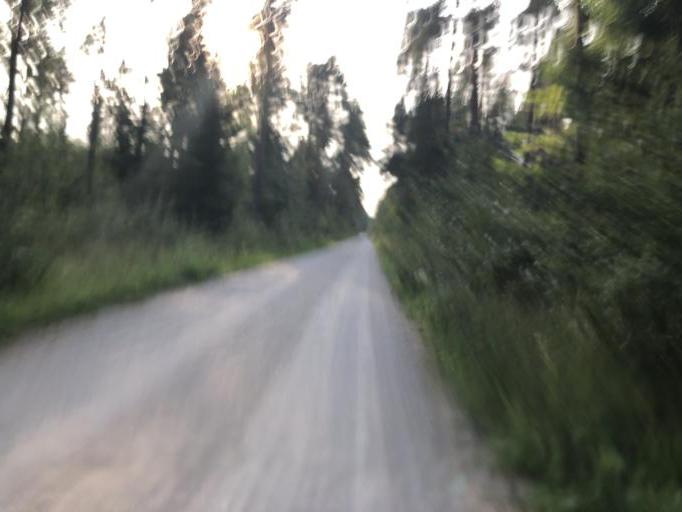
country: DE
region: Bavaria
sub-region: Regierungsbezirk Mittelfranken
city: Buckenhof
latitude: 49.5765
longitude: 11.0518
